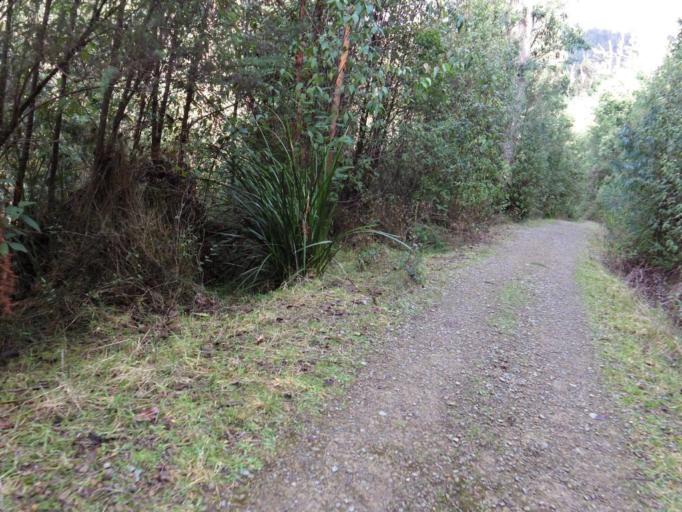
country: AU
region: Victoria
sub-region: Yarra Ranges
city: Millgrove
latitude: -37.5284
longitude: 145.7725
